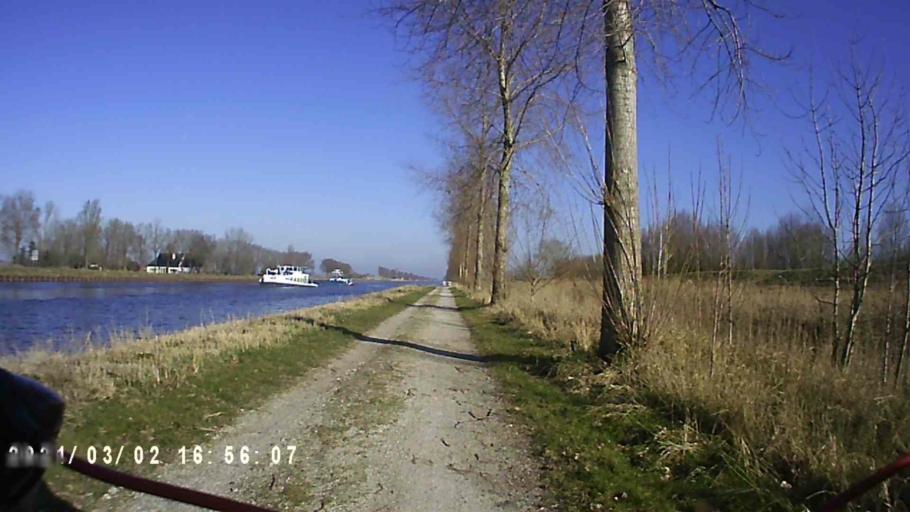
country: NL
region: Groningen
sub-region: Gemeente Grootegast
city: Grootegast
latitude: 53.2430
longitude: 6.2555
